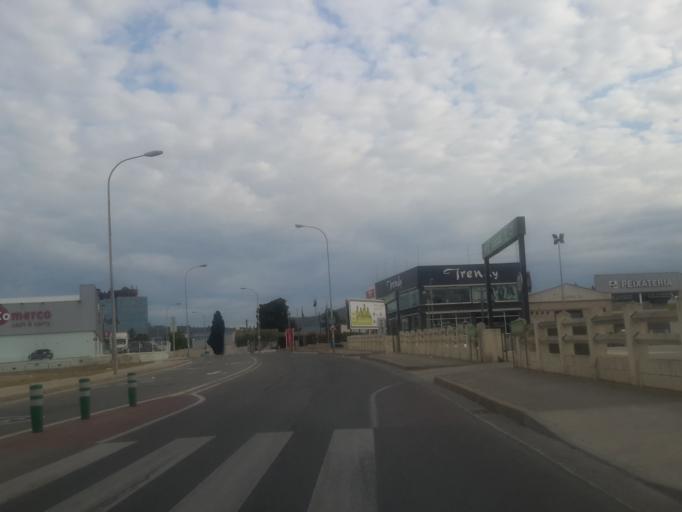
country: ES
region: Catalonia
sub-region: Provincia de Barcelona
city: Vilanova i la Geltru
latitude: 41.2264
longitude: 1.7400
